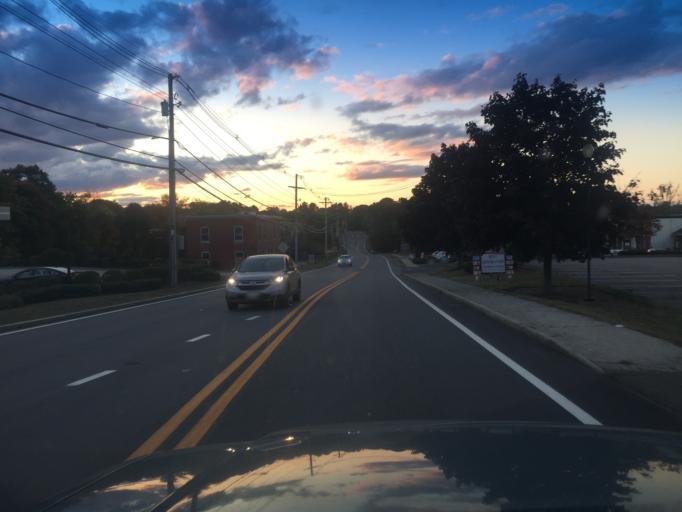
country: US
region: Massachusetts
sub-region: Norfolk County
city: Franklin
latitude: 42.0898
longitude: -71.4309
